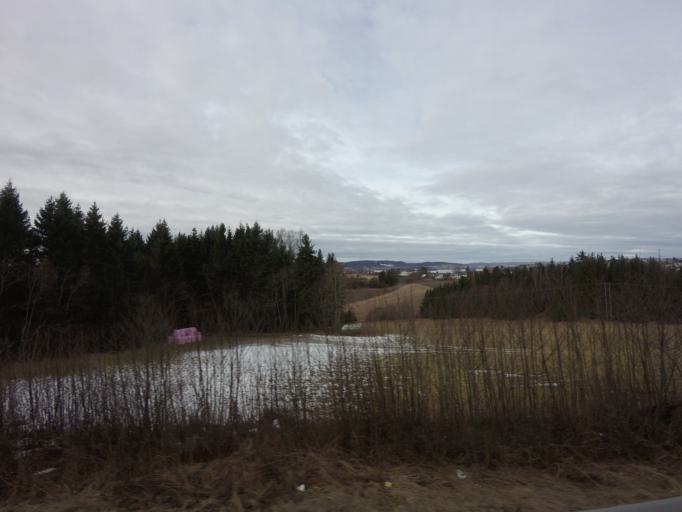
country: NO
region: Akershus
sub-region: Fet
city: Fetsund
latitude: 59.9144
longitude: 11.1841
